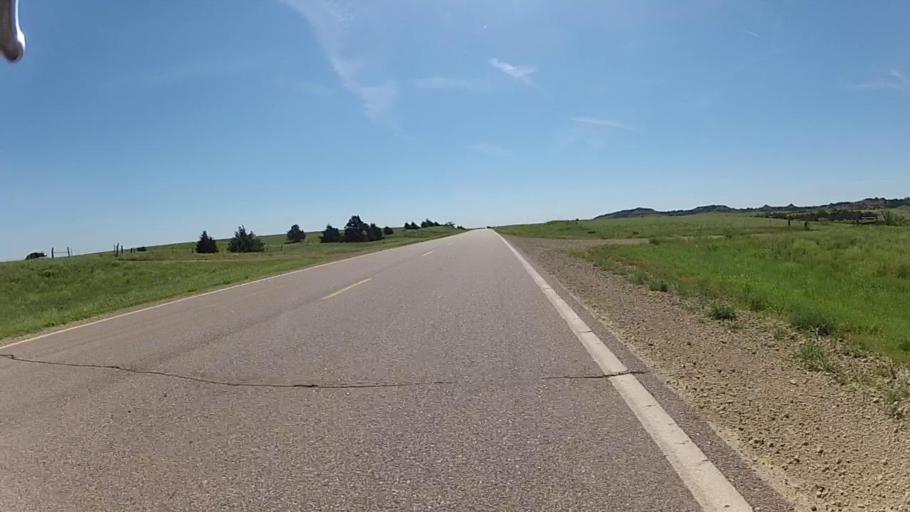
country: US
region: Kansas
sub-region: Barber County
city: Medicine Lodge
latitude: 37.2751
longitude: -98.7254
